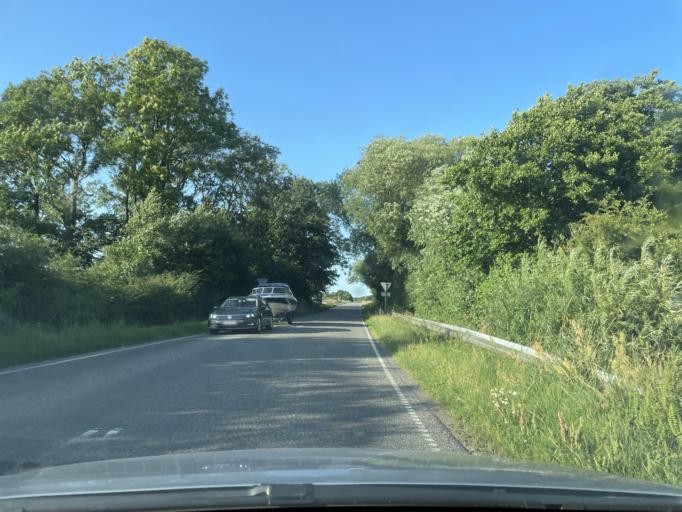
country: DK
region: South Denmark
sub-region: Tonder Kommune
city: Toftlund
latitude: 55.0676
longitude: 9.1566
